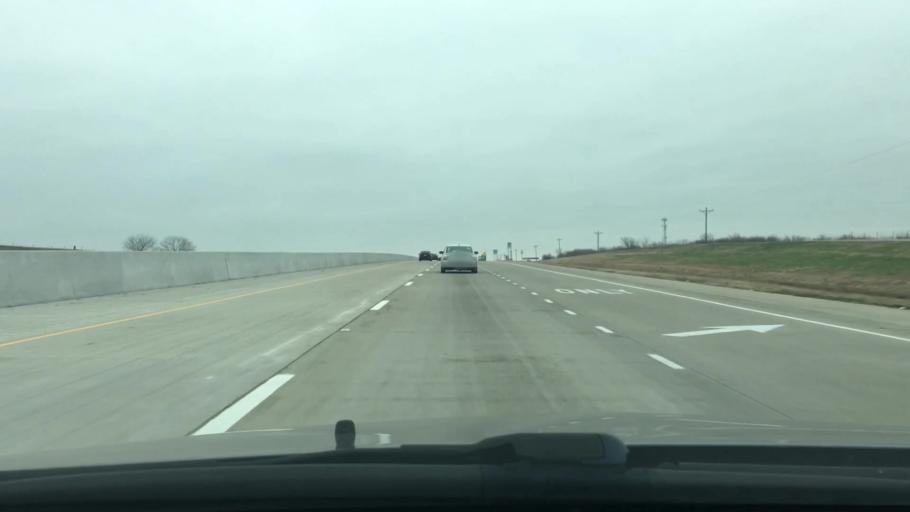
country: US
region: Texas
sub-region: Freestone County
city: Wortham
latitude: 31.8862
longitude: -96.3516
